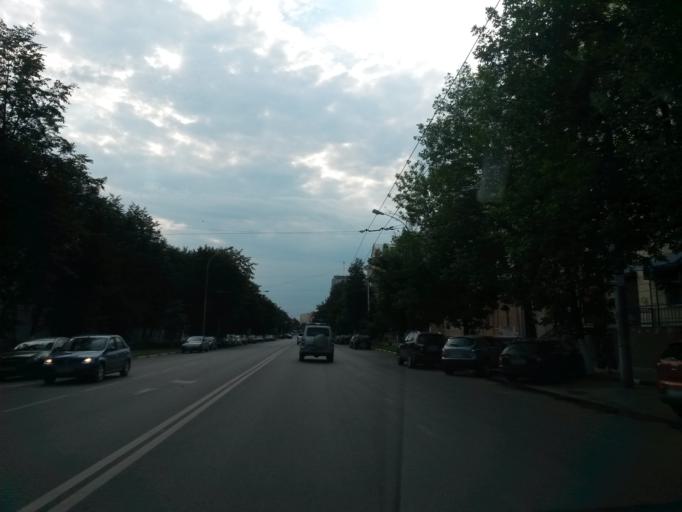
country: RU
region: Jaroslavl
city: Yaroslavl
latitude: 57.6266
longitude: 39.8569
